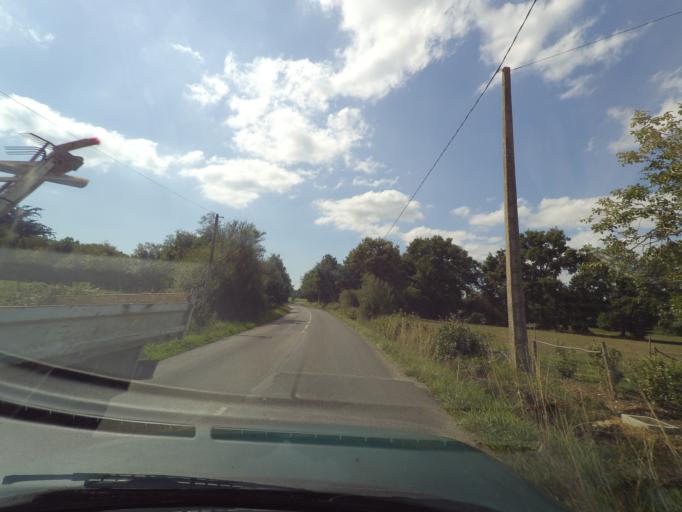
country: FR
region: Pays de la Loire
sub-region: Departement de la Loire-Atlantique
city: Sainte-Pazanne
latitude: 47.0989
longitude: -1.8327
